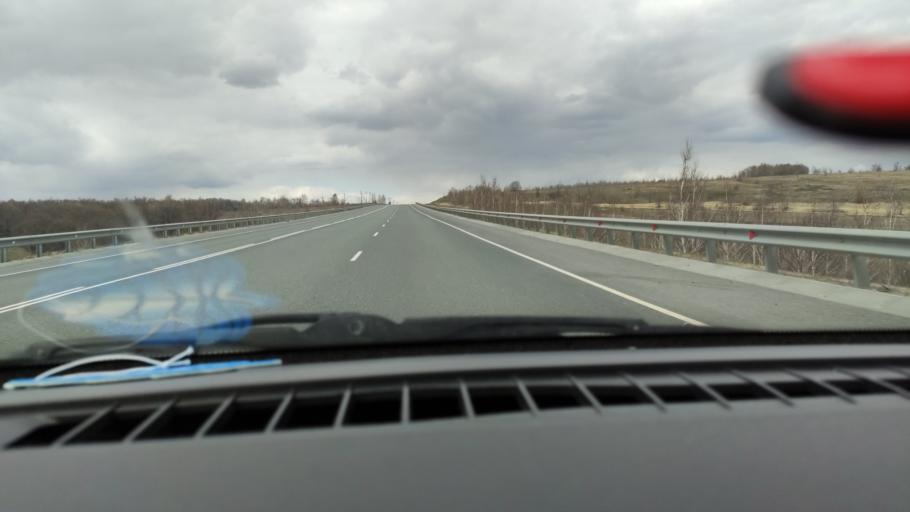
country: RU
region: Saratov
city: Shikhany
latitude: 52.1432
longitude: 47.2029
